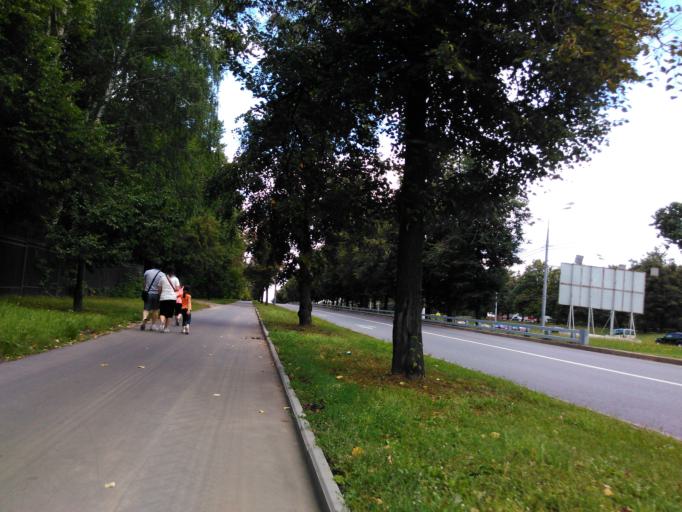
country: RU
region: Moscow
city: Luzhniki
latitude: 55.7025
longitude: 37.5479
